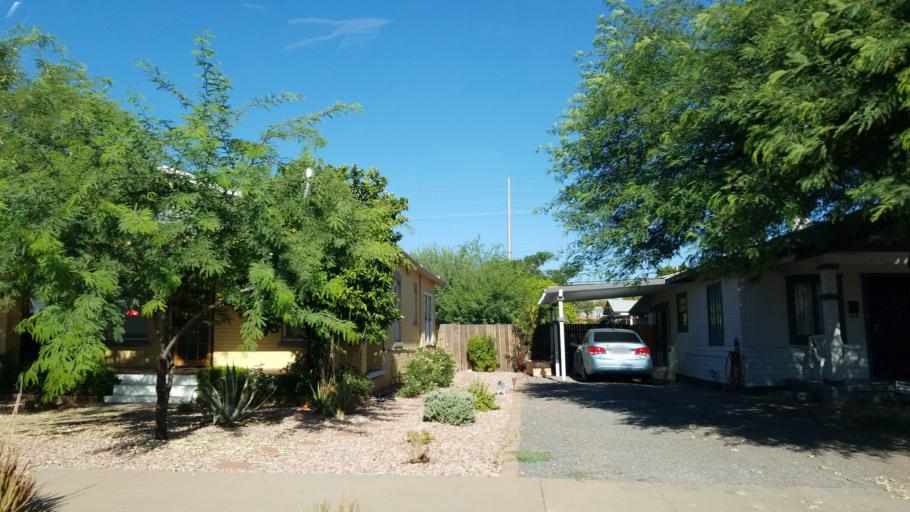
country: US
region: Arizona
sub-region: Maricopa County
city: Phoenix
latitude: 33.4702
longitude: -112.0640
